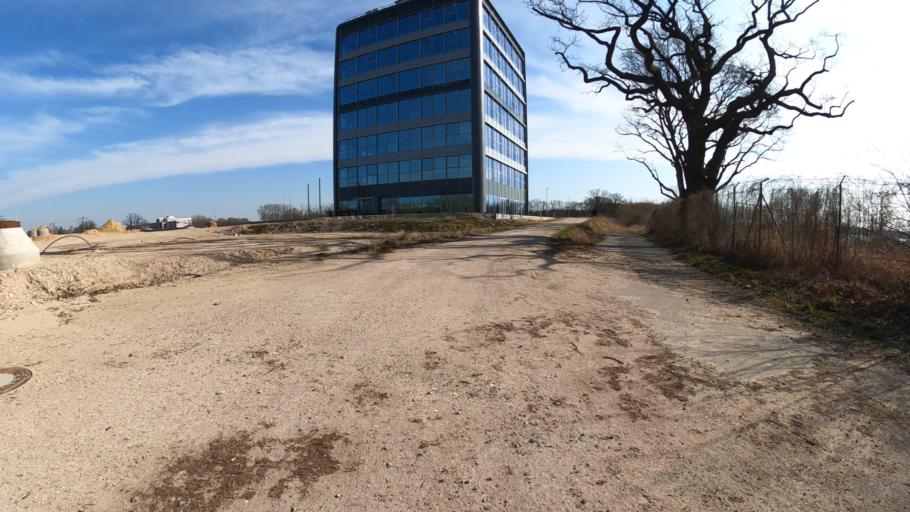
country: DE
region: Schleswig-Holstein
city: Wedel
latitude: 53.5666
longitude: 9.7296
